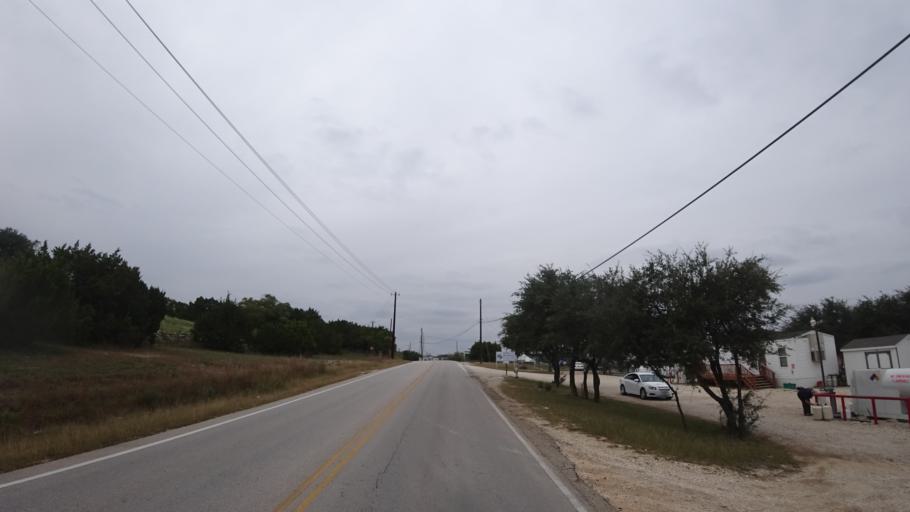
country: US
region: Texas
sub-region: Travis County
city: Lakeway
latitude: 30.3748
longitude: -97.9393
